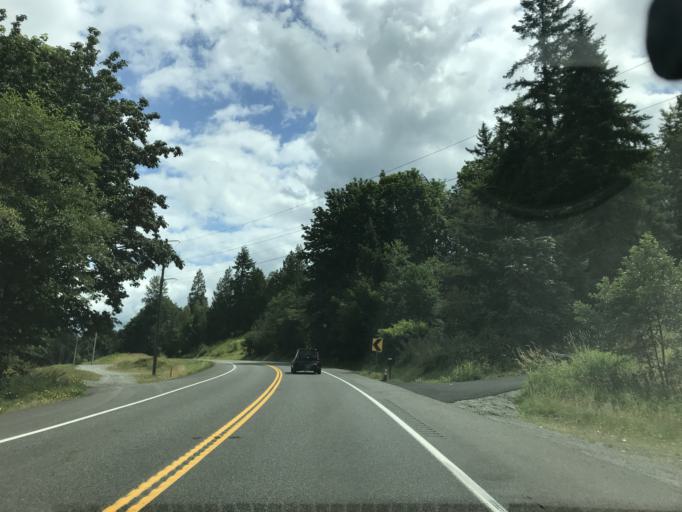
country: US
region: Washington
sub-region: King County
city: Maple Heights-Lake Desire
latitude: 47.4215
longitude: -122.0800
